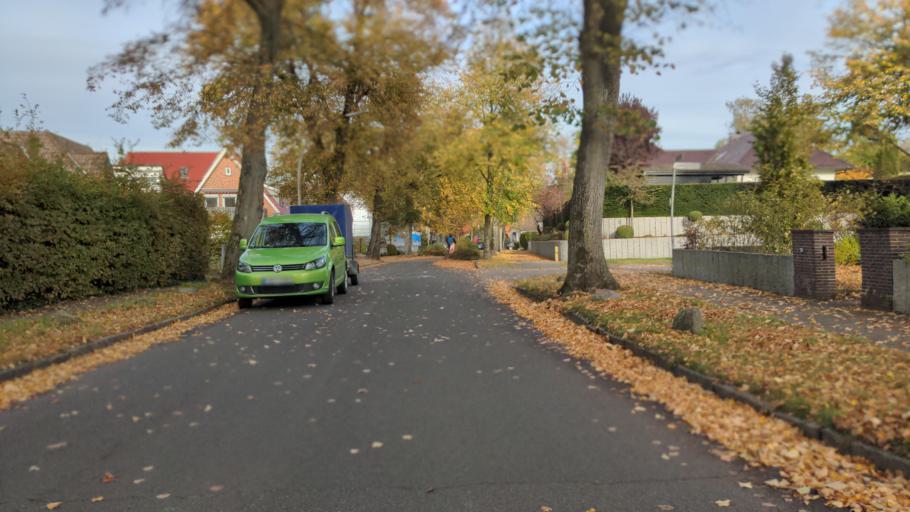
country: DE
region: Schleswig-Holstein
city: Bad Schwartau
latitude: 53.9112
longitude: 10.6877
